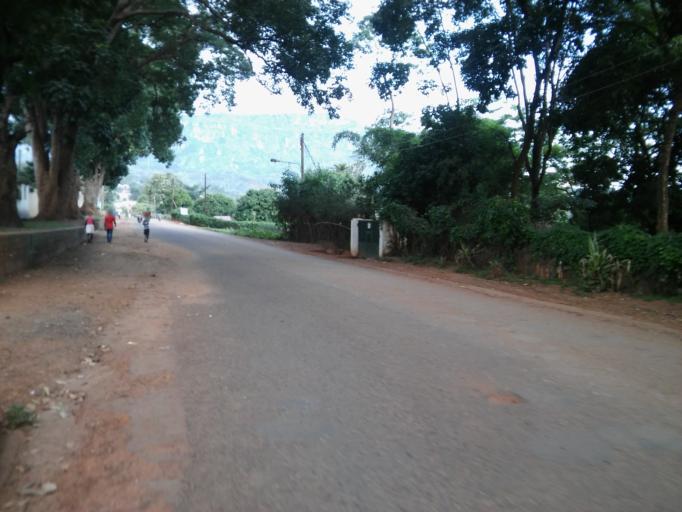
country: UG
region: Eastern Region
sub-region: Mbale District
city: Mbale
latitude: 1.0639
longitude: 34.1987
